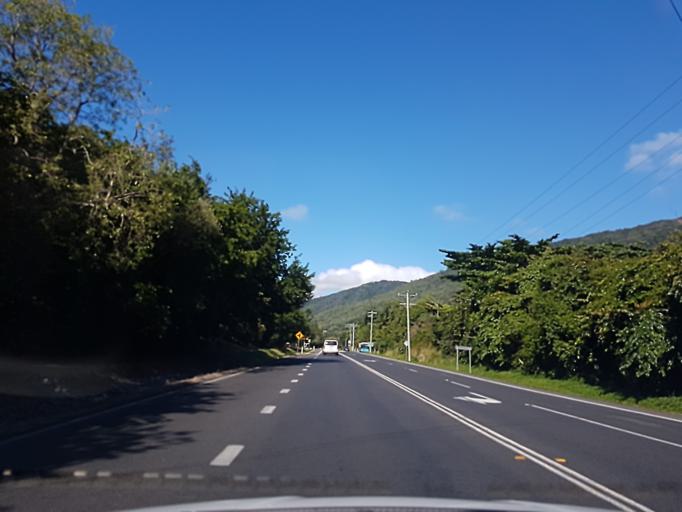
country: AU
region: Queensland
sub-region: Cairns
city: Palm Cove
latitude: -16.7456
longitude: 145.6635
